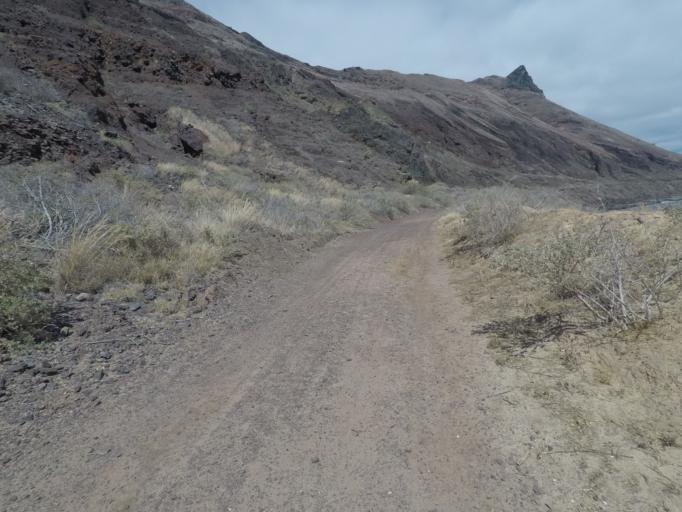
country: PT
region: Madeira
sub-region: Porto Santo
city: Vila de Porto Santo
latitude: 33.0629
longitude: -16.3052
